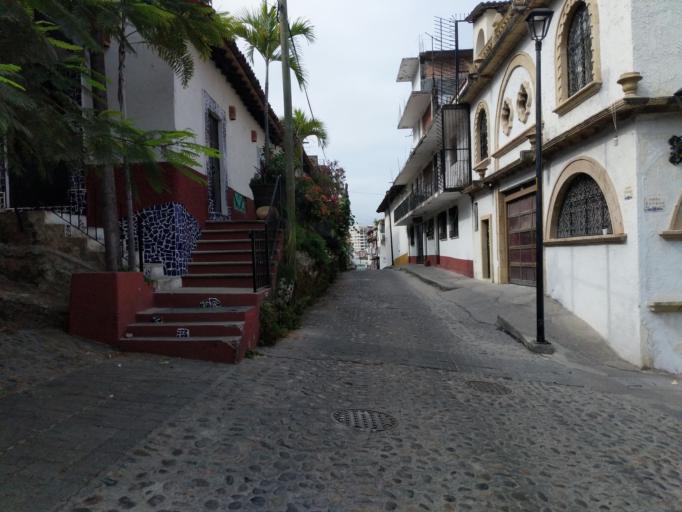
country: MX
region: Jalisco
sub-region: Puerto Vallarta
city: Puerto Vallarta
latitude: 20.6102
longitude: -105.2336
